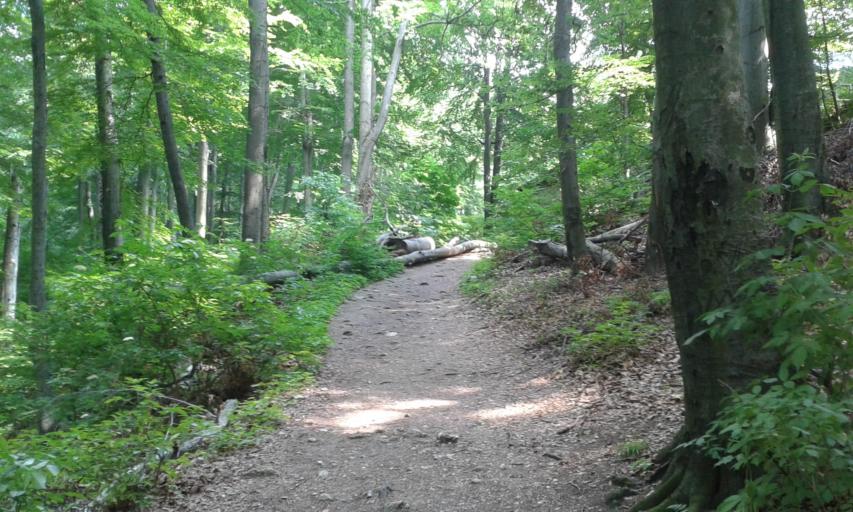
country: PL
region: Lesser Poland Voivodeship
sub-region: Powiat chrzanowski
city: Babice
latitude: 50.0775
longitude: 19.4452
